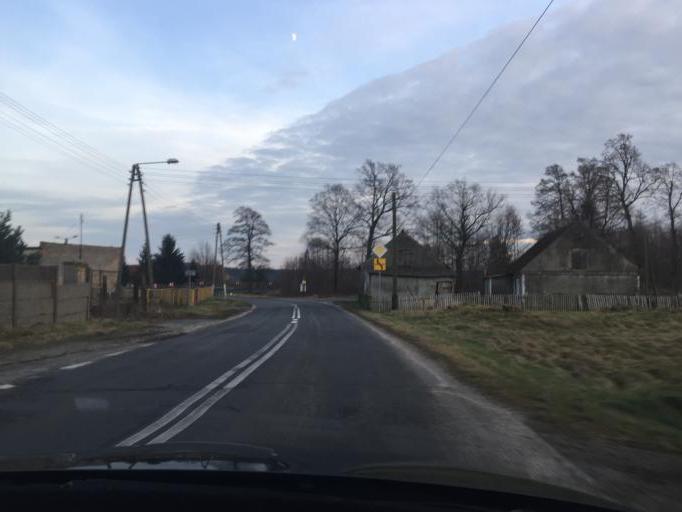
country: PL
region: Lubusz
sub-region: Powiat zielonogorski
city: Ochla
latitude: 51.8004
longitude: 15.4886
